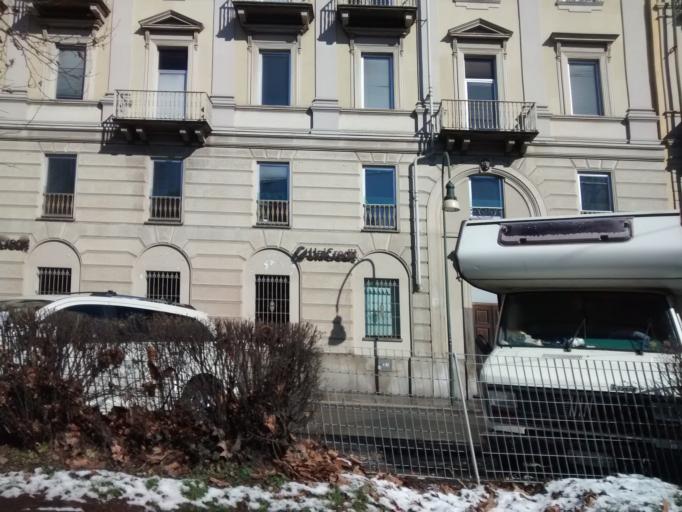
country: IT
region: Piedmont
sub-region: Provincia di Torino
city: Turin
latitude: 45.0588
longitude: 7.6898
